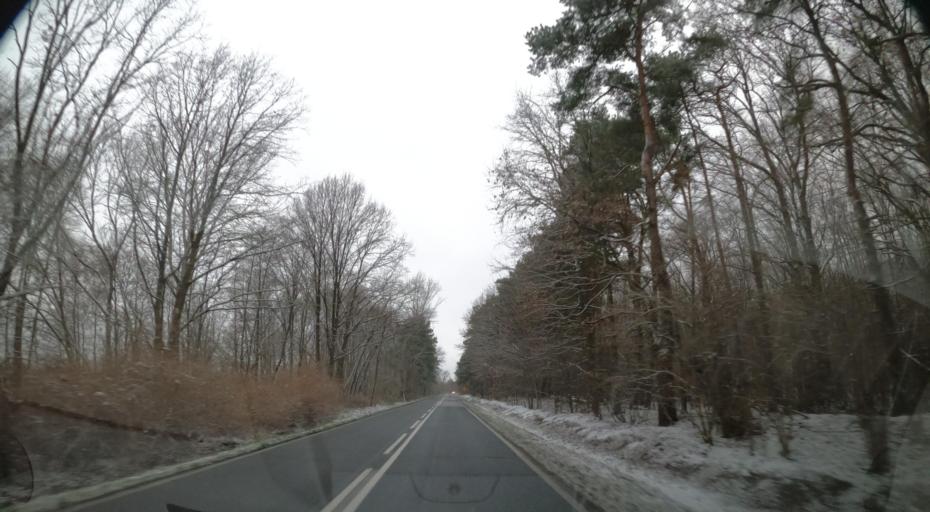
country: PL
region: Masovian Voivodeship
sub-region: Powiat plocki
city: Maszewo Duze
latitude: 52.5742
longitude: 19.5559
